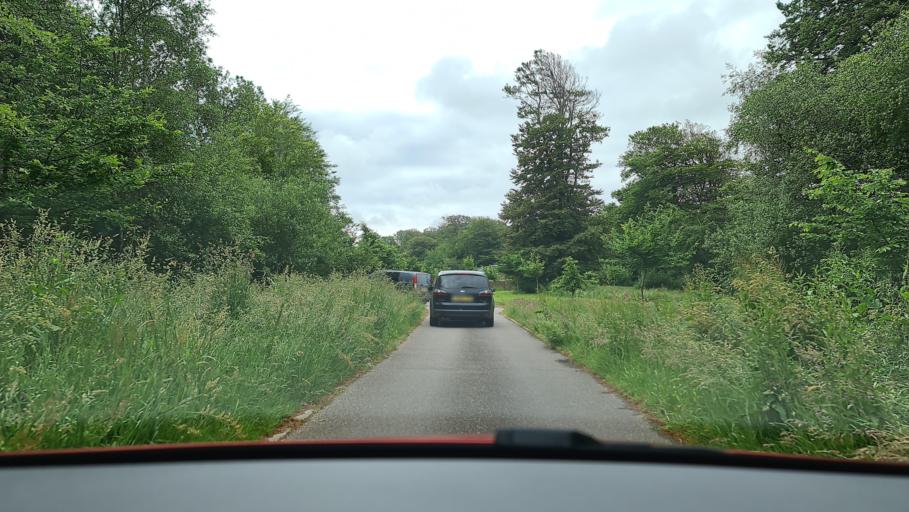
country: GB
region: England
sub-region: Cornwall
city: Bodmin
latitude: 50.4481
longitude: -4.6957
